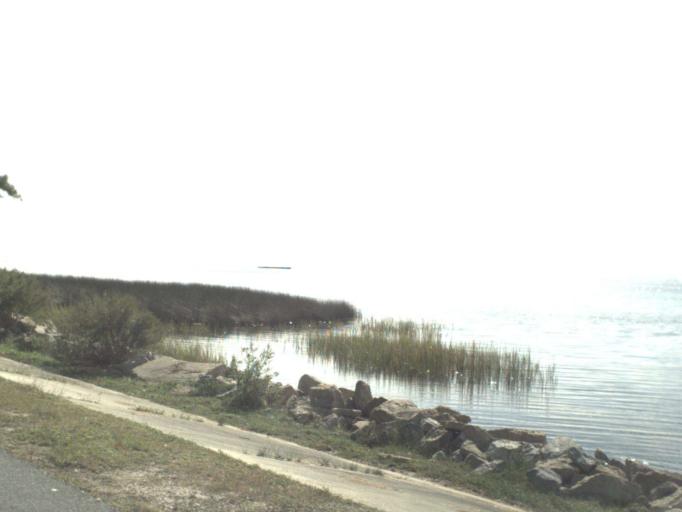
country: US
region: Florida
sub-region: Gulf County
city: Port Saint Joe
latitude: 29.7939
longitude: -85.3017
